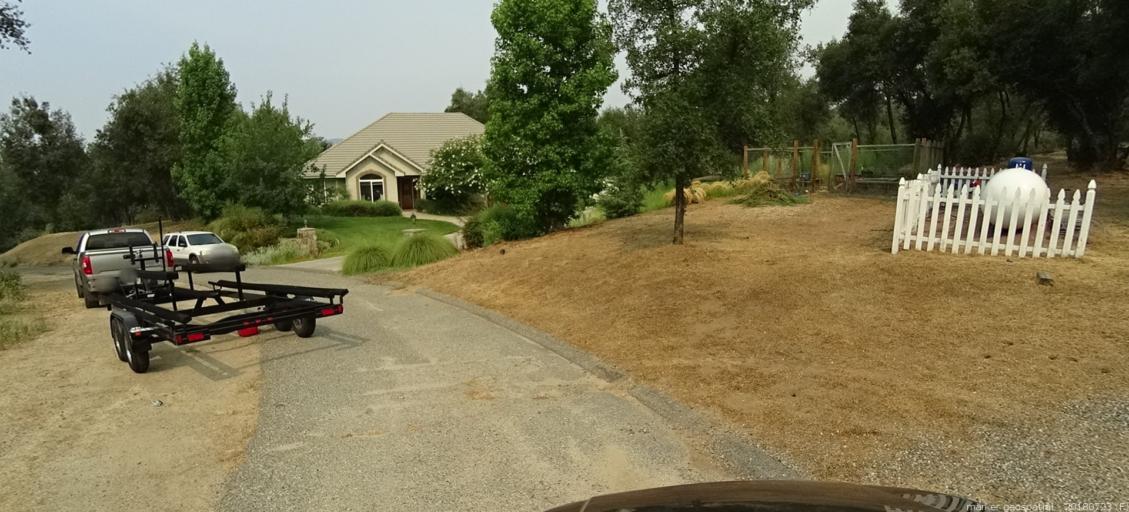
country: US
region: California
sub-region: Madera County
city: Ahwahnee
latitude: 37.3738
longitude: -119.6972
